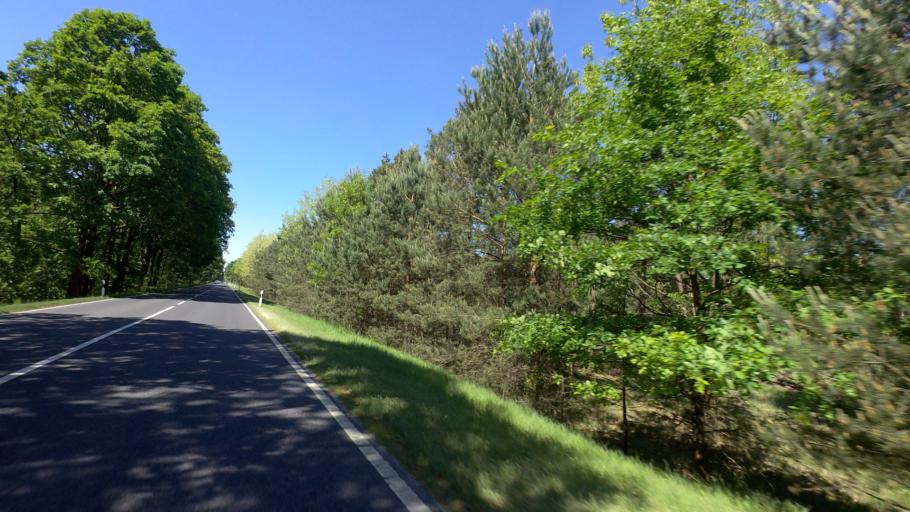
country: DE
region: Brandenburg
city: Lieberose
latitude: 51.9560
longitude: 14.3292
